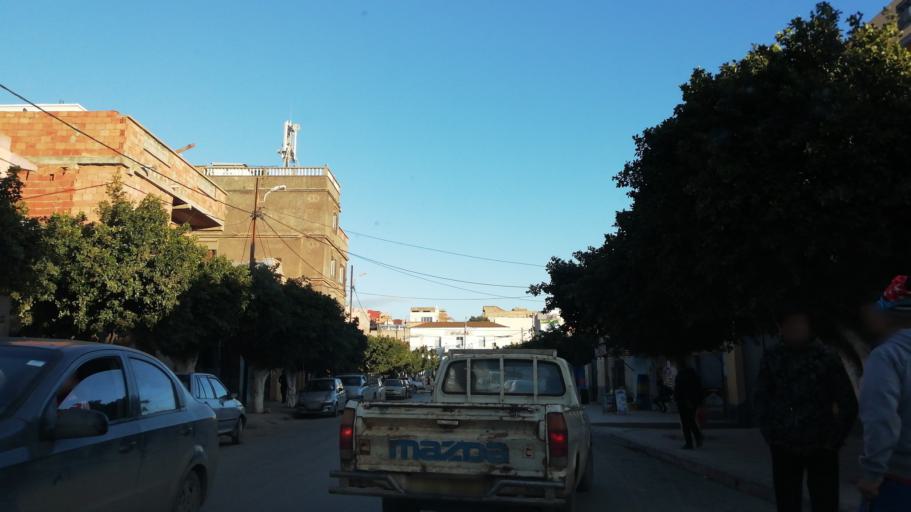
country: DZ
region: Oran
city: Sidi ech Chahmi
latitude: 35.6921
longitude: -0.5029
